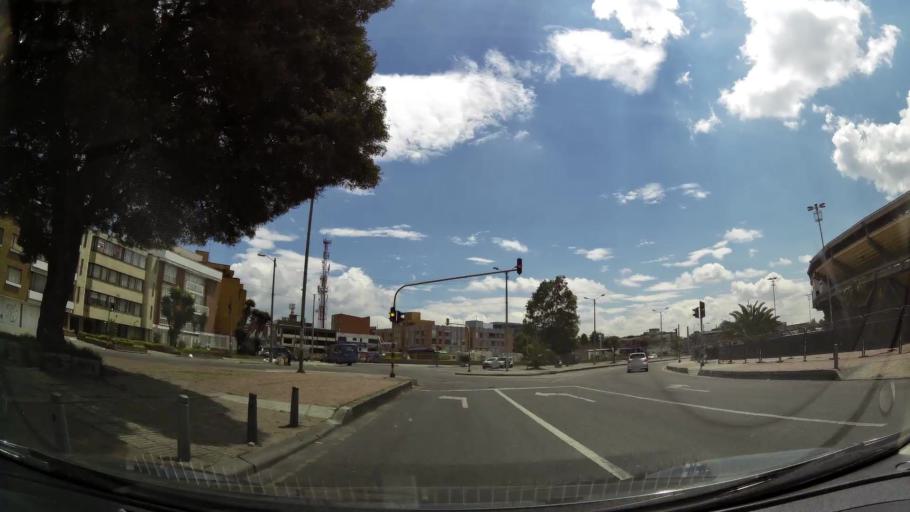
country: CO
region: Bogota D.C.
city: Bogota
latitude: 4.6449
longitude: -74.0767
